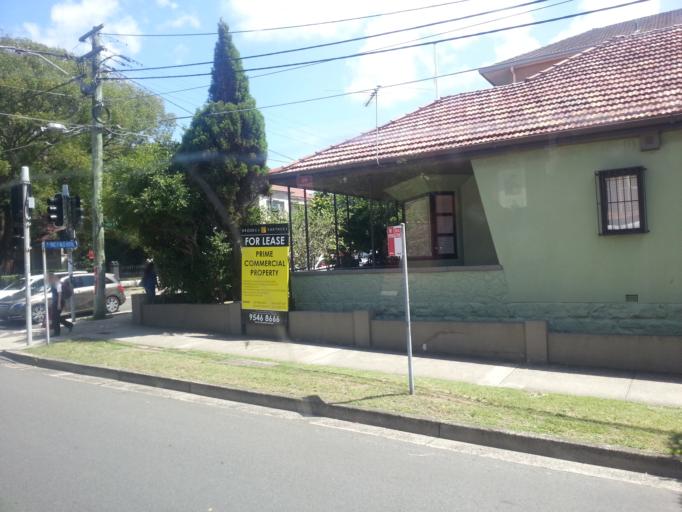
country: AU
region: New South Wales
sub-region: Randwick
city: Kingsford
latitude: -33.9165
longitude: 151.2368
